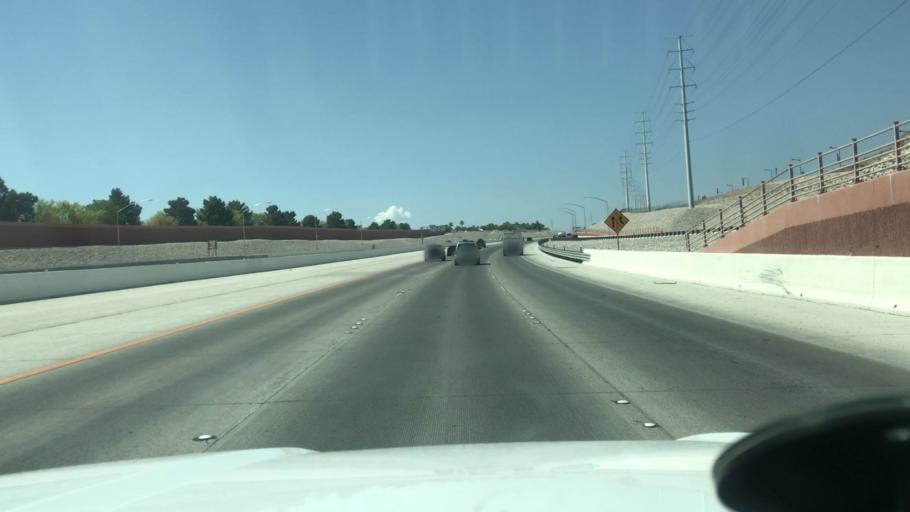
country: US
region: Nevada
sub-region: Clark County
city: Summerlin South
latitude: 36.2185
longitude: -115.3285
